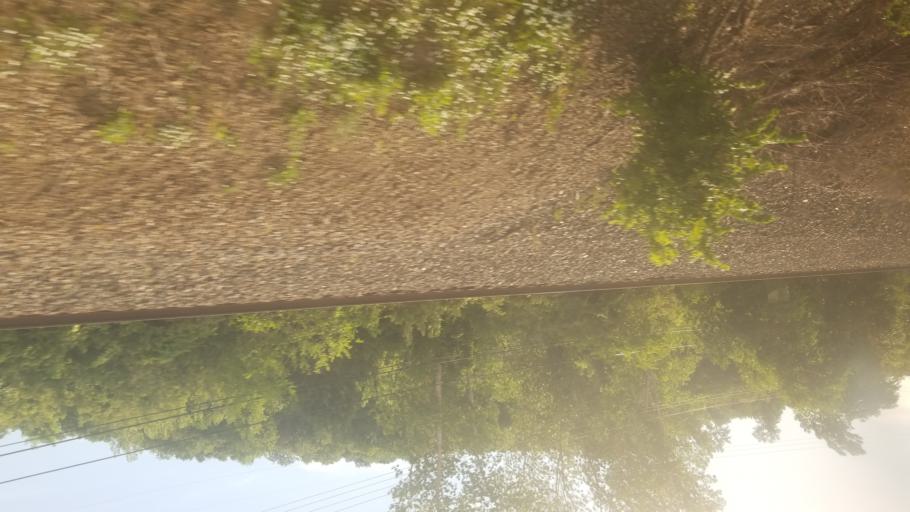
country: US
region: Kansas
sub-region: Wyandotte County
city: Edwardsville
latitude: 39.0444
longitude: -94.7879
